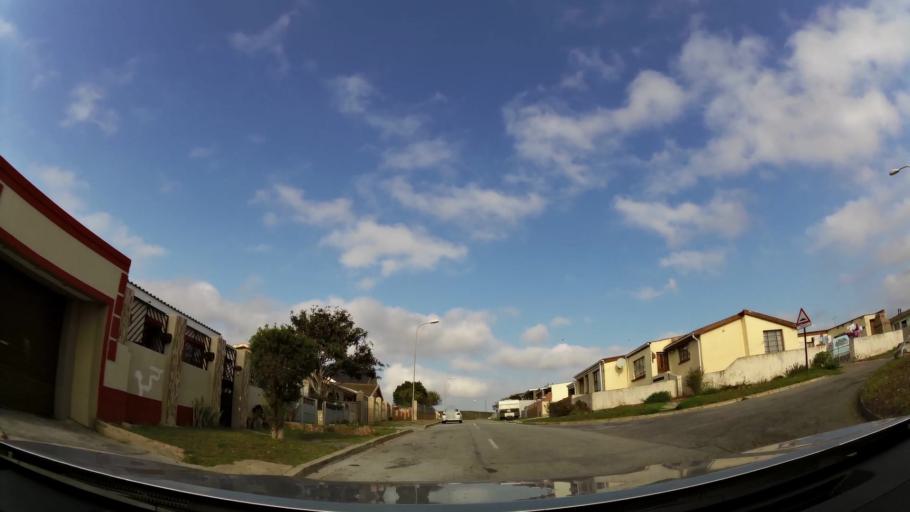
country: ZA
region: Eastern Cape
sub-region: Nelson Mandela Bay Metropolitan Municipality
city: Port Elizabeth
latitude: -33.9219
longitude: 25.5501
